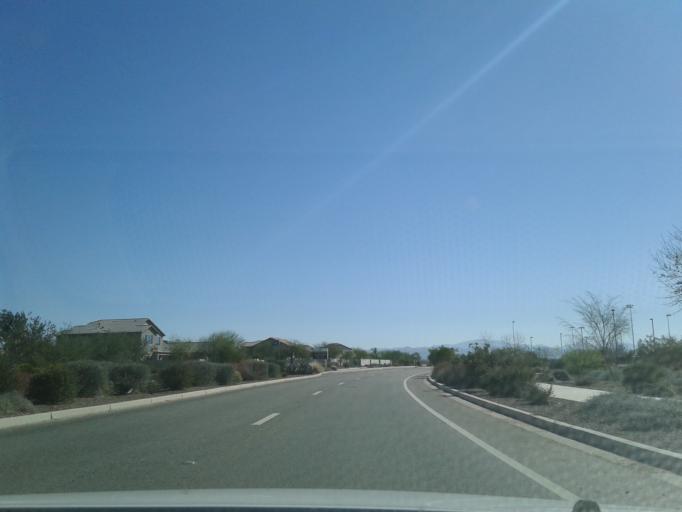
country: US
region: Arizona
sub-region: Pima County
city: Avra Valley
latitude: 32.5710
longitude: -111.3334
